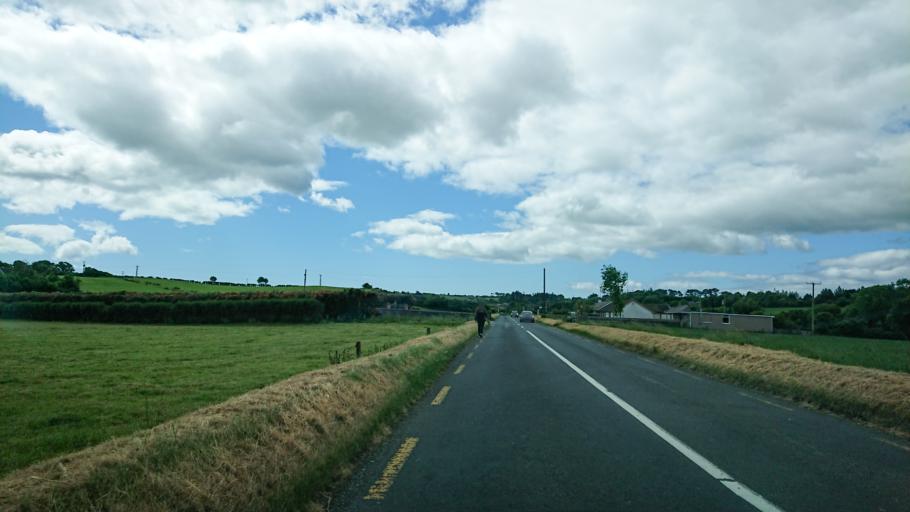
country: IE
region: Leinster
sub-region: Kilkenny
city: Mooncoin
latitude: 52.2283
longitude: -7.1998
